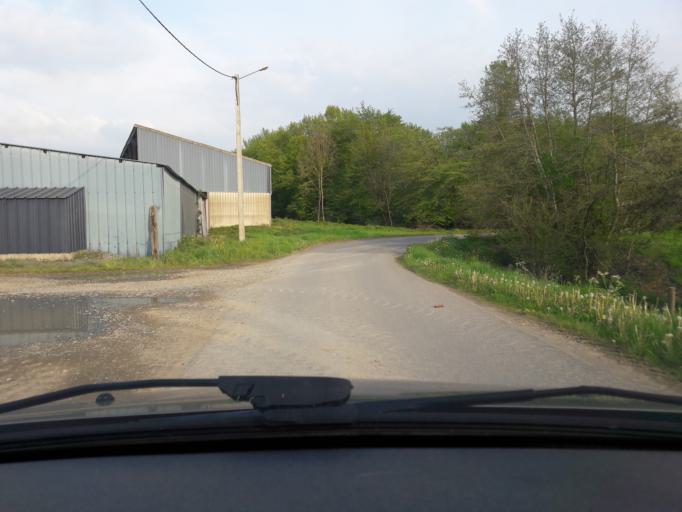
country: FR
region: Nord-Pas-de-Calais
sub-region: Departement du Nord
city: Marpent
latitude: 50.2396
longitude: 4.0786
